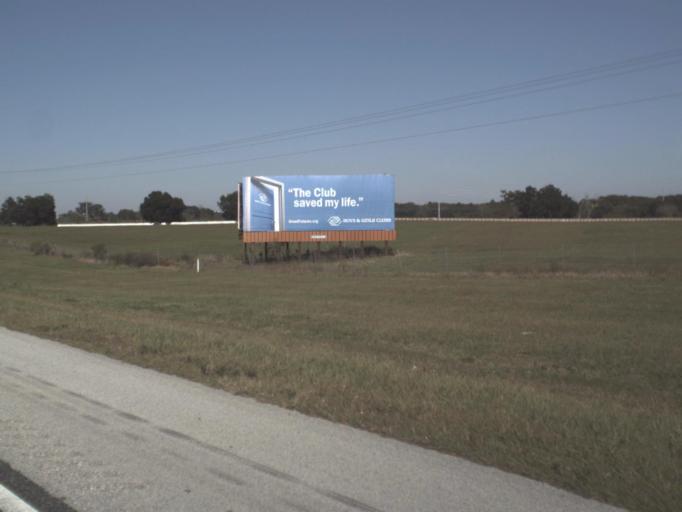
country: US
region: Florida
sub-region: Sumter County
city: Wildwood
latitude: 28.7923
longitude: -81.9910
